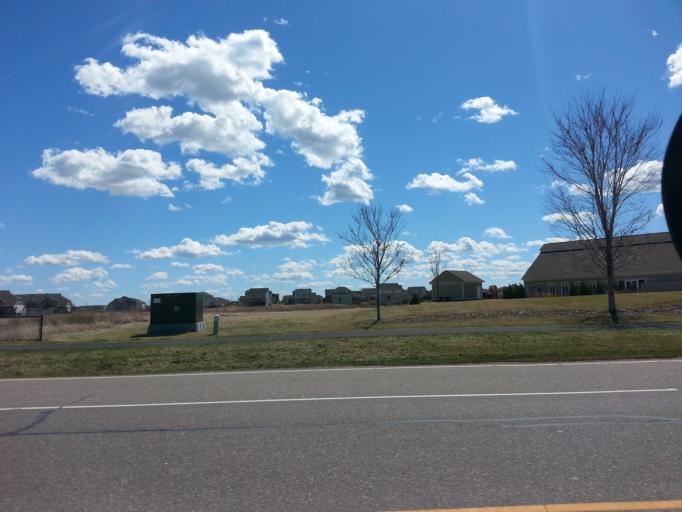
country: US
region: Minnesota
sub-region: Dakota County
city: Apple Valley
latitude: 44.7140
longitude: -93.1804
